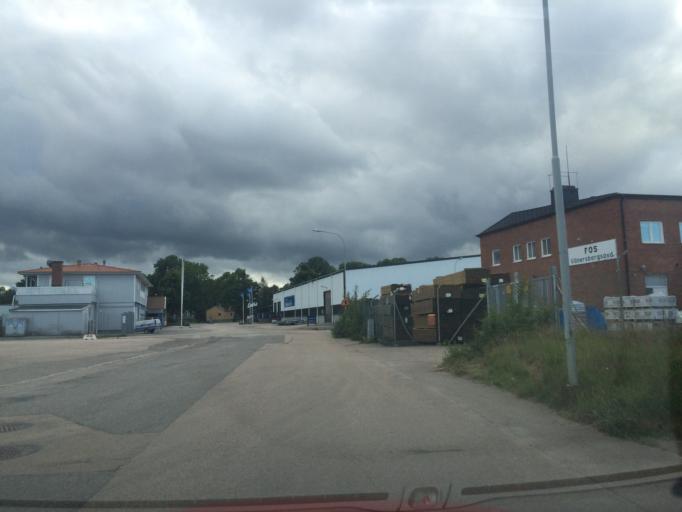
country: SE
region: Vaestra Goetaland
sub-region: Vanersborgs Kommun
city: Vanersborg
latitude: 58.3784
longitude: 12.3410
